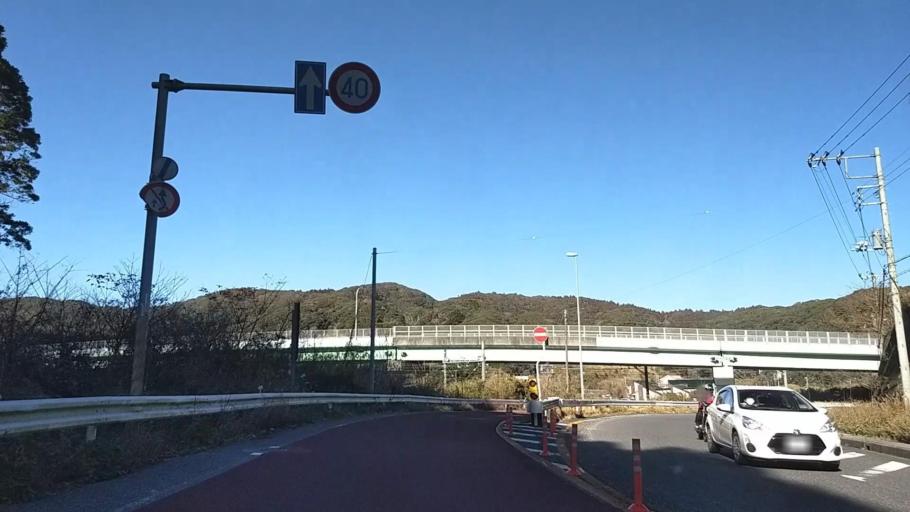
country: JP
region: Chiba
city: Katsuura
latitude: 35.1645
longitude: 140.3272
